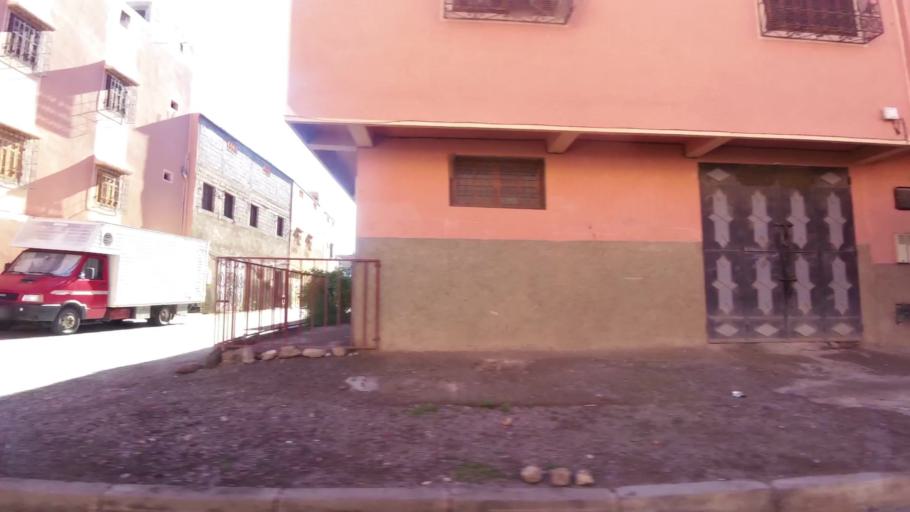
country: MA
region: Marrakech-Tensift-Al Haouz
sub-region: Marrakech
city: Marrakesh
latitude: 31.5937
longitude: -8.0247
